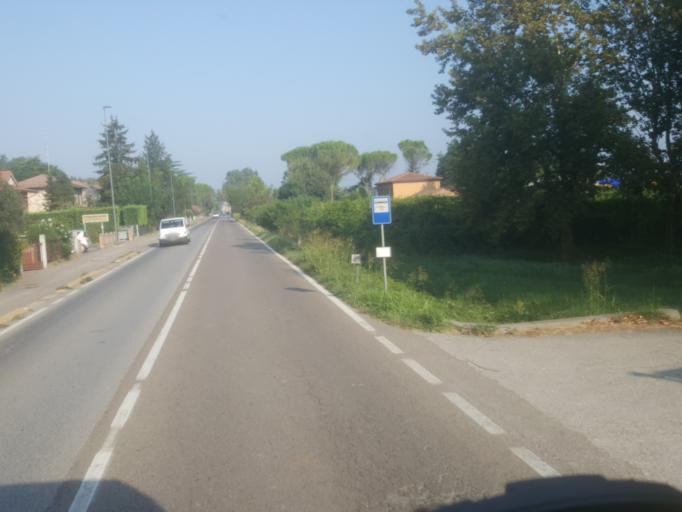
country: IT
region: Emilia-Romagna
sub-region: Provincia di Ravenna
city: Mezzano
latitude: 44.4616
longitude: 12.0957
